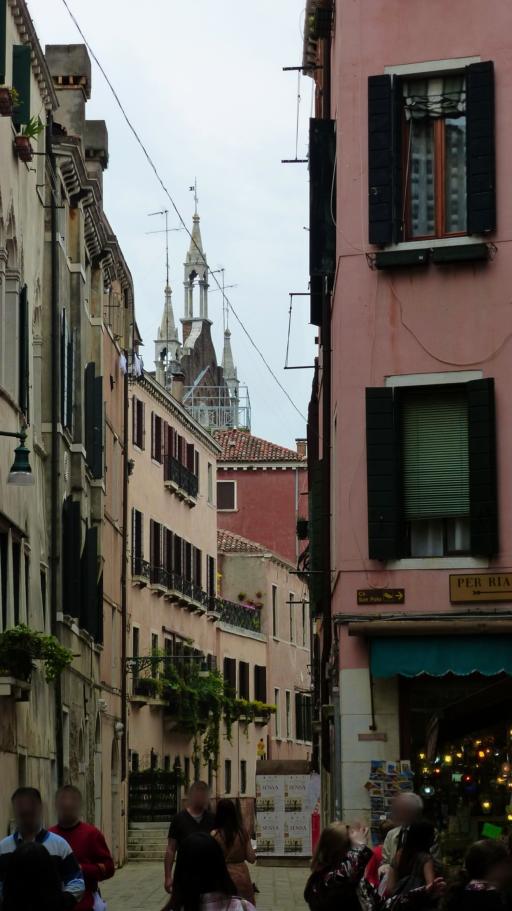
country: IT
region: Veneto
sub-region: Provincia di Venezia
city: Venice
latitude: 45.4365
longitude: 12.3285
